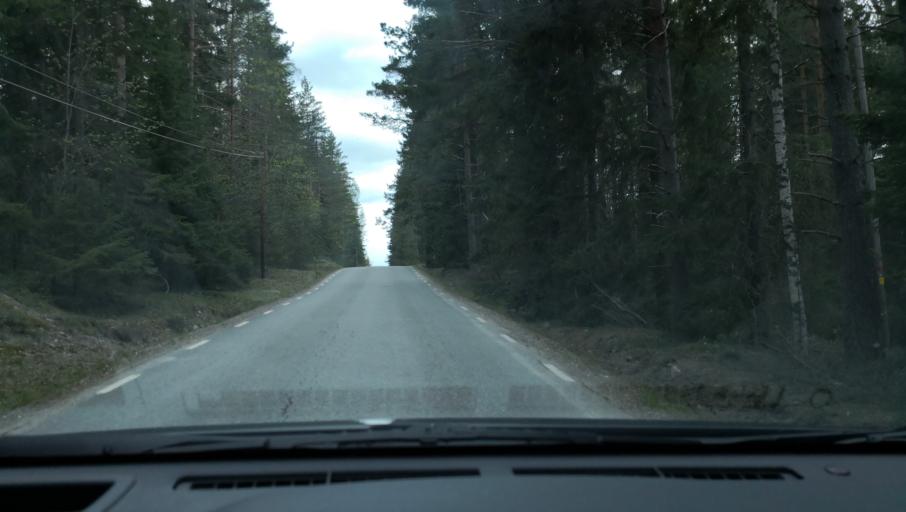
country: SE
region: Vaestmanland
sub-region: Norbergs Kommun
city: Norberg
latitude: 60.0893
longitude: 15.8728
